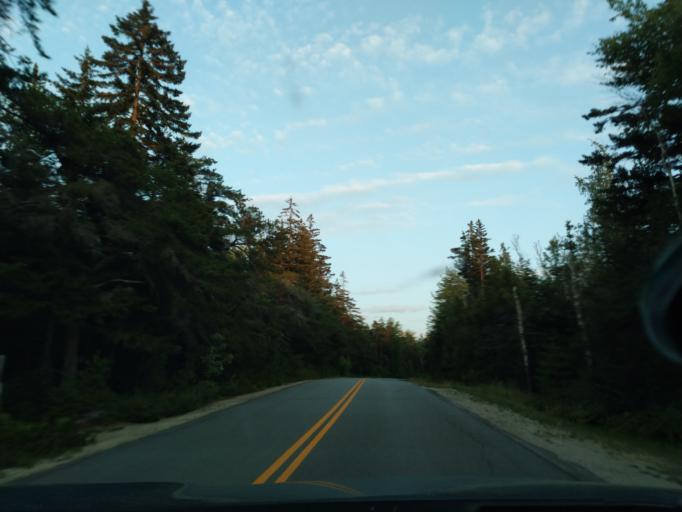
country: US
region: Maine
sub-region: Hancock County
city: Gouldsboro
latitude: 44.3894
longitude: -68.0719
